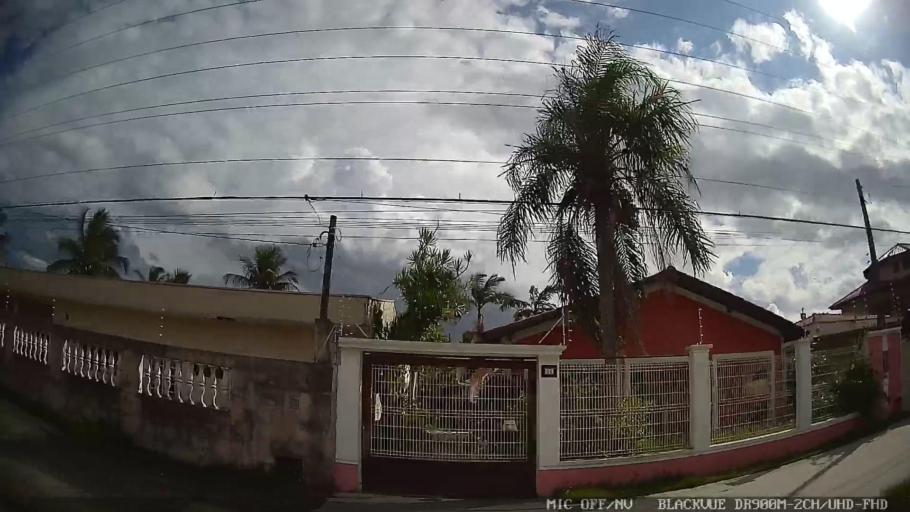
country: BR
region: Sao Paulo
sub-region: Caraguatatuba
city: Caraguatatuba
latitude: -23.6352
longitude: -45.4202
